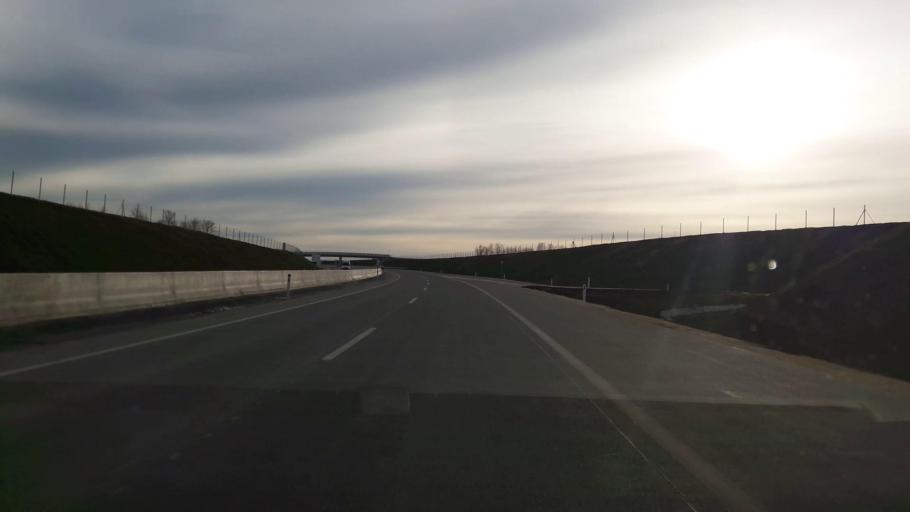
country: AT
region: Lower Austria
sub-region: Politischer Bezirk Mistelbach
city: Herrnbaumgarten
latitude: 48.7046
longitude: 16.6515
